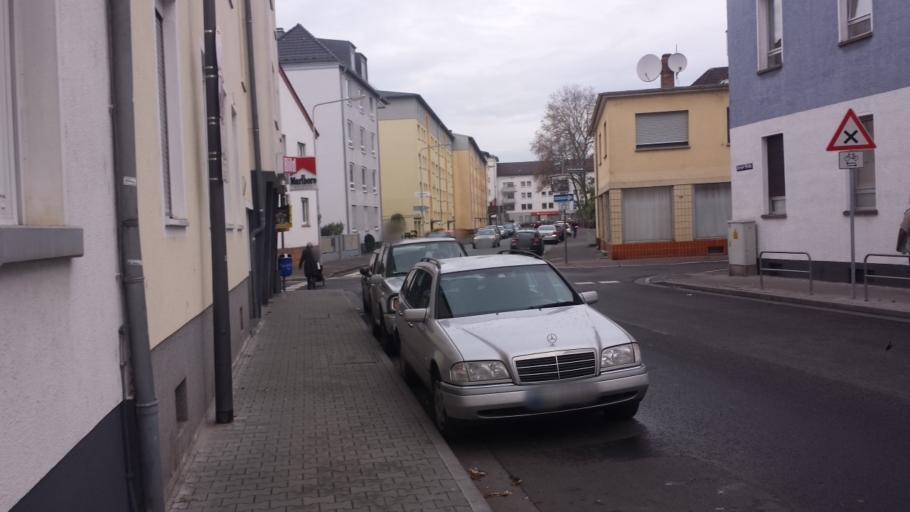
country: DE
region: Hesse
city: Niederrad
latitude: 50.0847
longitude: 8.6435
